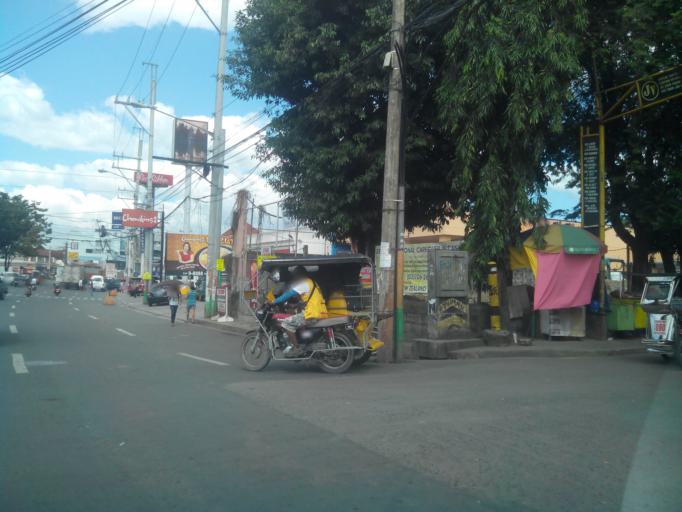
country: PH
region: Calabarzon
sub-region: Province of Rizal
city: Taytay
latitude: 14.5575
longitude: 121.1365
